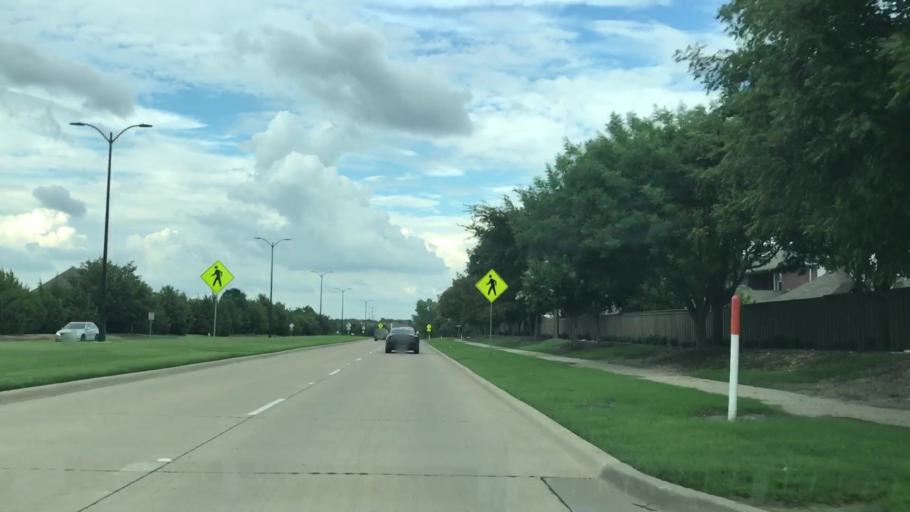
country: US
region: Texas
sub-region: Collin County
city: Frisco
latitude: 33.1776
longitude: -96.7851
